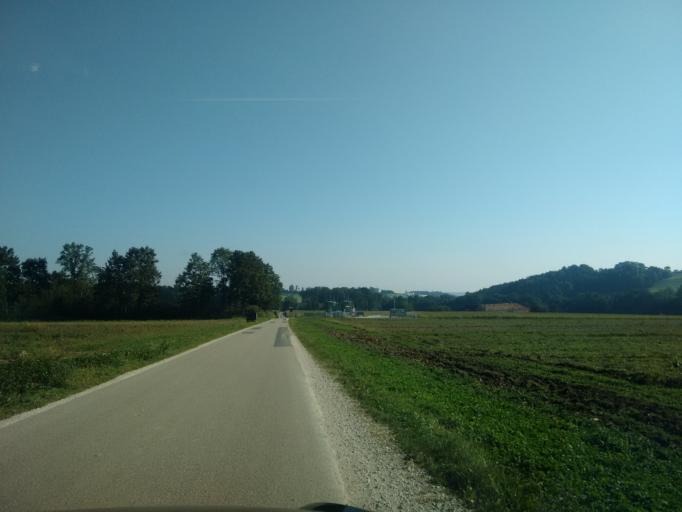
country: AT
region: Upper Austria
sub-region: Wels-Land
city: Marchtrenk
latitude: 48.1334
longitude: 14.1923
